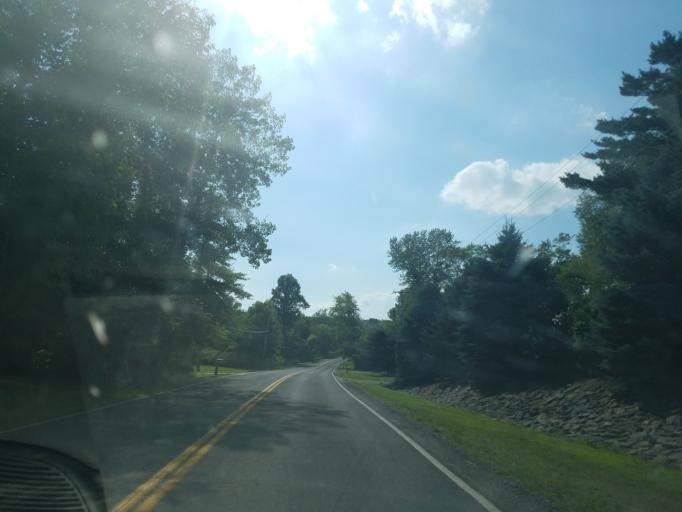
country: US
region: Ohio
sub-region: Summit County
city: Mogadore
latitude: 41.0437
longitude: -81.3551
